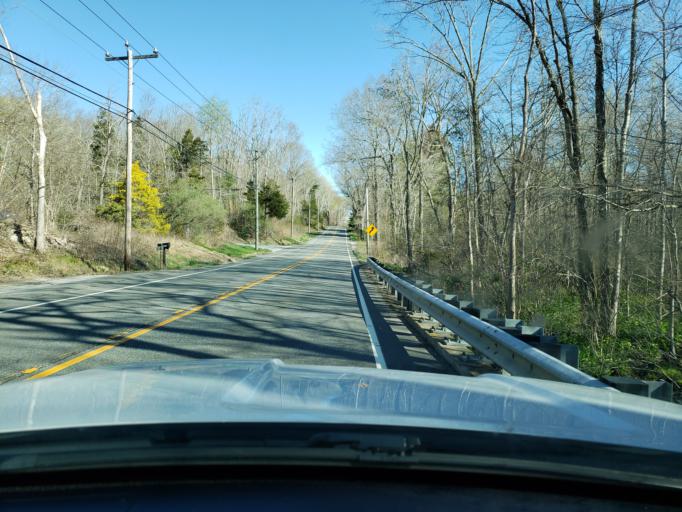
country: US
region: Connecticut
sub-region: New London County
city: Colchester
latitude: 41.5044
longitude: -72.2878
